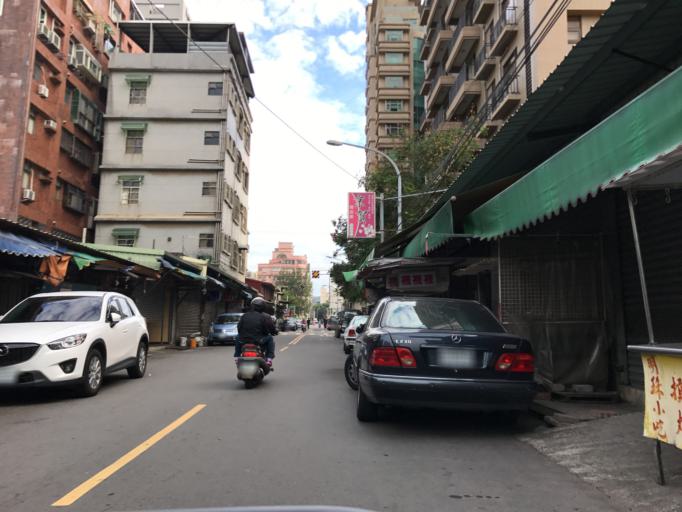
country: TW
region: Taiwan
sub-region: Hsinchu
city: Hsinchu
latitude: 24.8108
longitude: 120.9715
